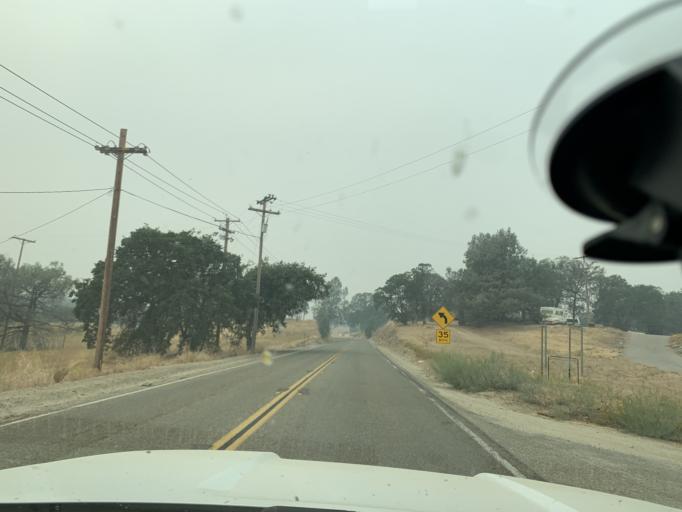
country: US
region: California
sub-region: Fresno County
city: Auberry
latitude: 37.0680
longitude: -119.4919
